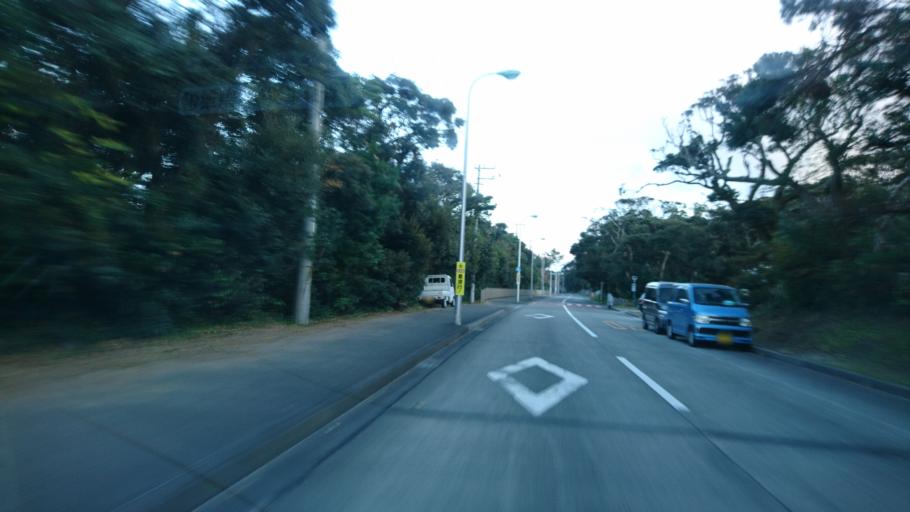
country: JP
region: Shizuoka
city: Shimoda
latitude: 34.3694
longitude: 139.2566
